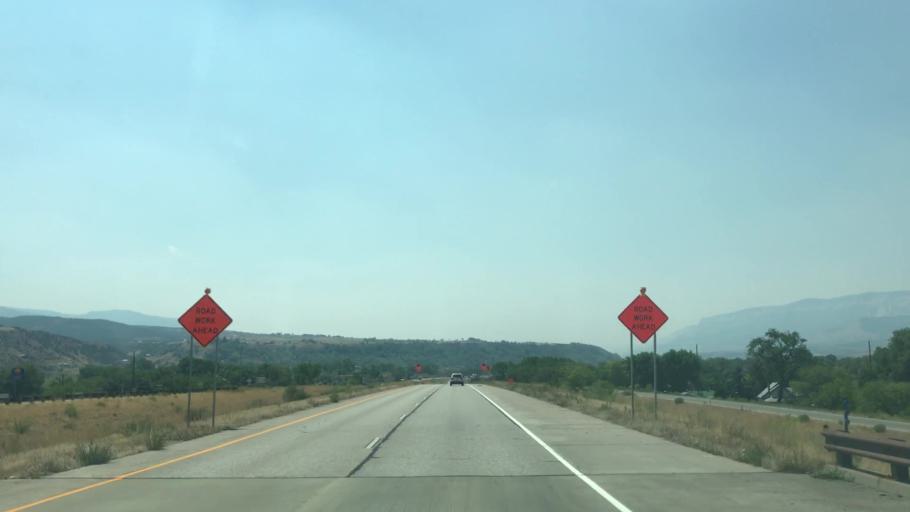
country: US
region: Colorado
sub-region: Garfield County
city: Rifle
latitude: 39.5242
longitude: -107.7777
